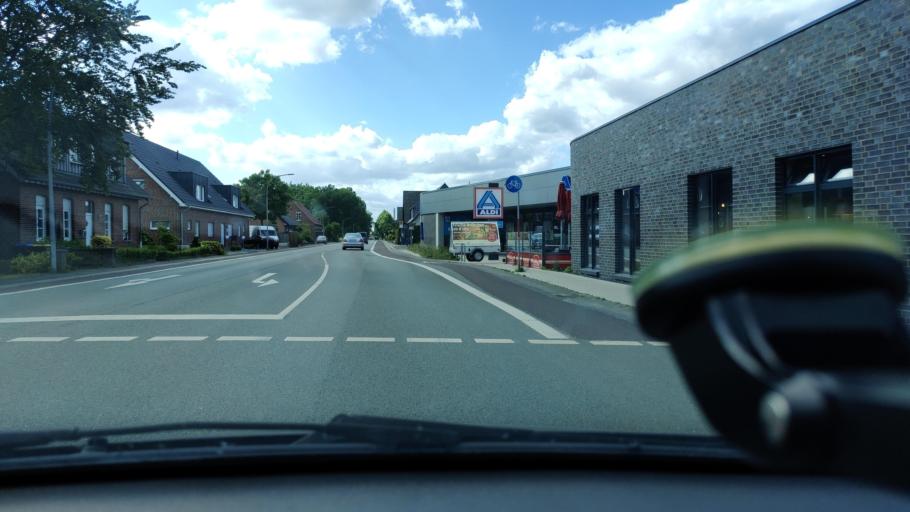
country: DE
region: North Rhine-Westphalia
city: Stadtlohn
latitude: 51.9869
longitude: 6.9419
